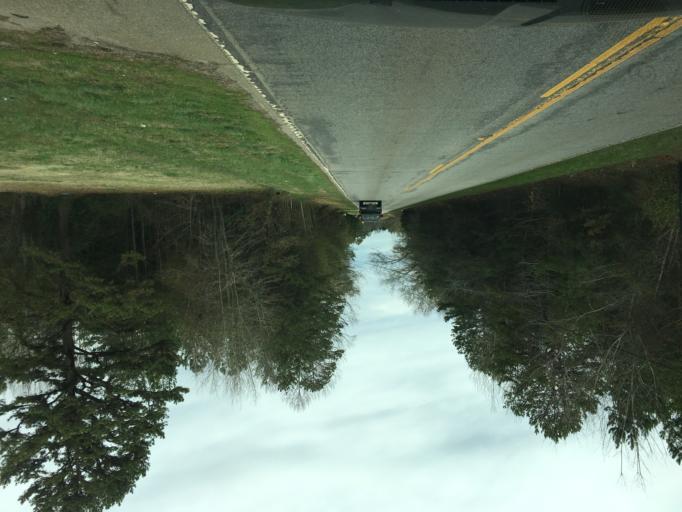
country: US
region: South Carolina
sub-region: Anderson County
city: Piedmont
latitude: 34.7025
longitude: -82.4327
